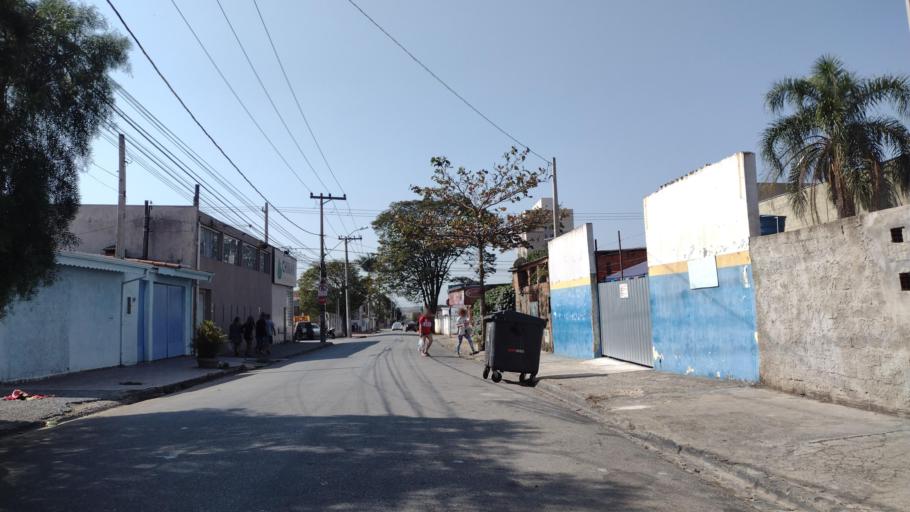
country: BR
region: Sao Paulo
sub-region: Sorocaba
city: Sorocaba
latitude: -23.4222
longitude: -47.4149
